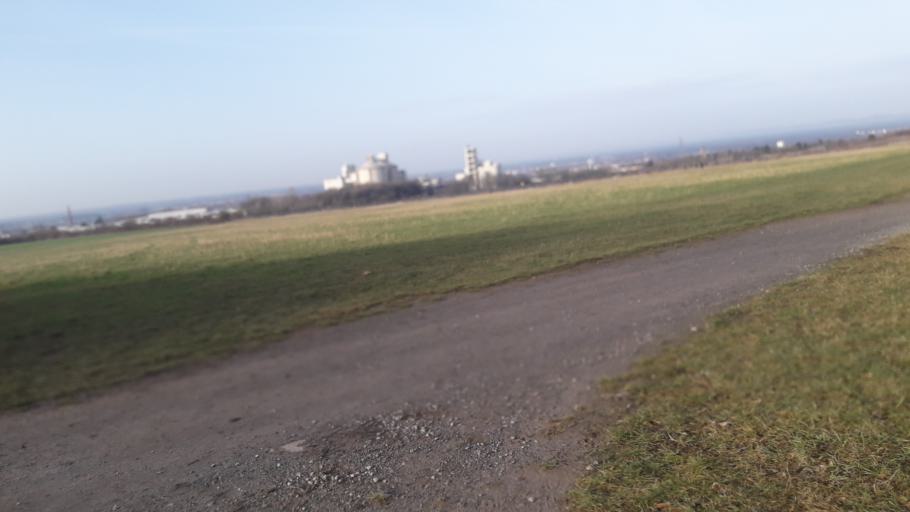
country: DE
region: North Rhine-Westphalia
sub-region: Regierungsbezirk Detmold
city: Paderborn
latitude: 51.6916
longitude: 8.7535
